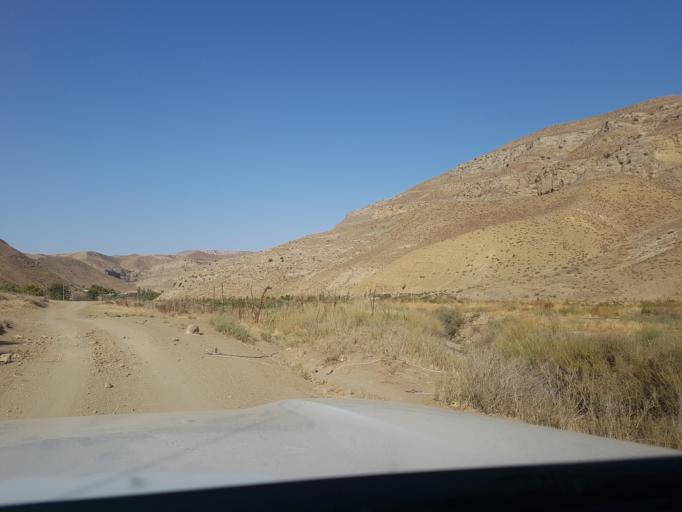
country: TM
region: Balkan
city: Magtymguly
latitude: 38.3007
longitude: 56.7570
